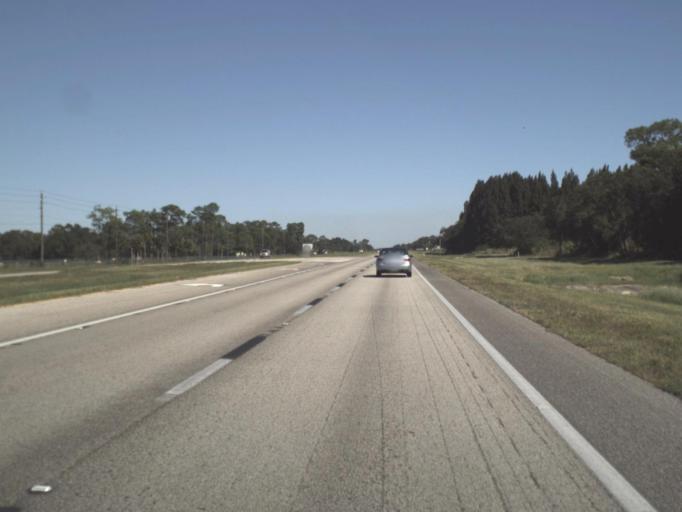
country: US
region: Florida
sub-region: Lee County
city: Alva
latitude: 26.7095
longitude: -81.5511
